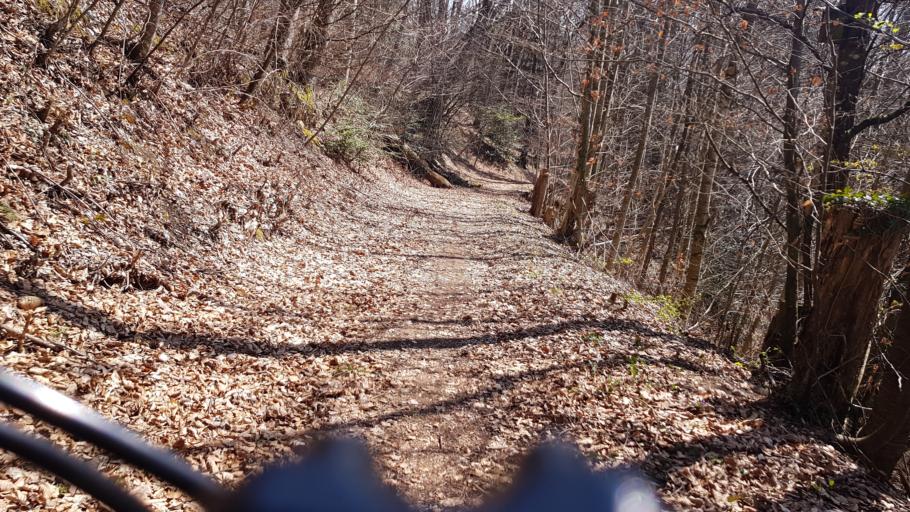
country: CH
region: Aargau
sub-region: Bezirk Kulm
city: Reinach
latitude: 47.2742
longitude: 8.1790
